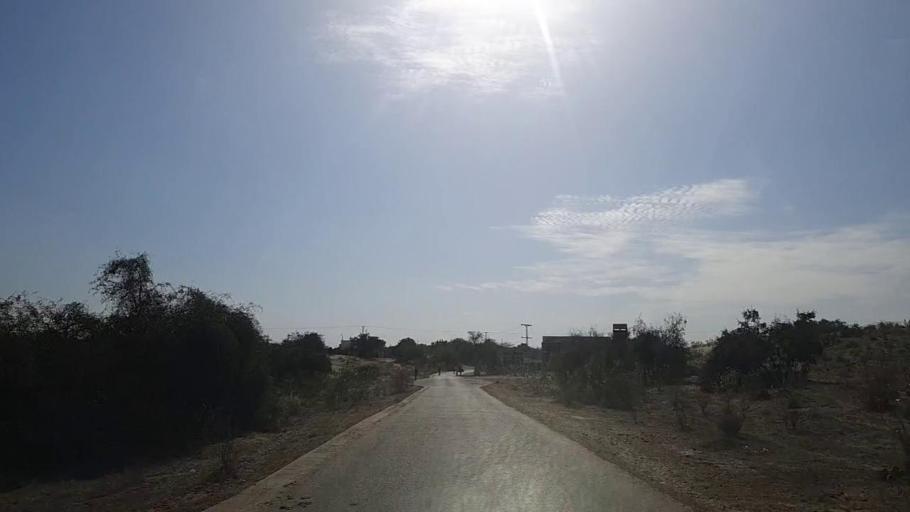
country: PK
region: Sindh
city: Naukot
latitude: 24.8422
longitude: 69.5423
